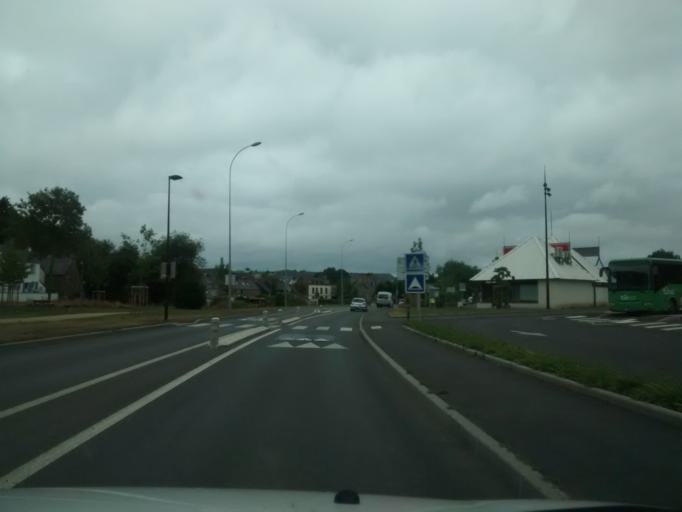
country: FR
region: Brittany
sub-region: Departement des Cotes-d'Armor
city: Lannion
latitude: 48.7264
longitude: -3.4557
